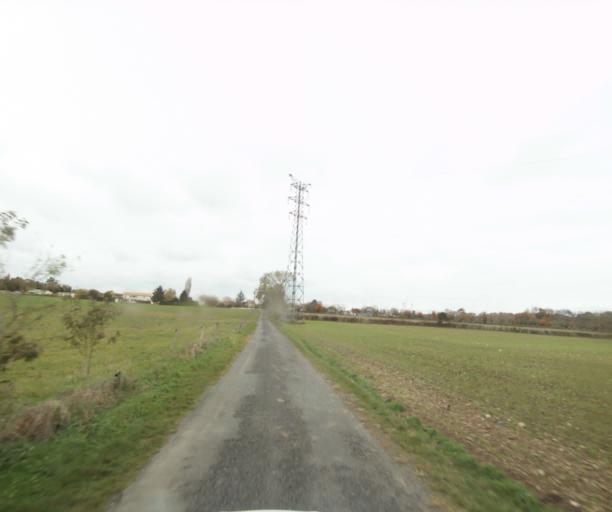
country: FR
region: Poitou-Charentes
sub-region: Departement de la Charente-Maritime
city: Saintes
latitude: 45.7659
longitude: -0.6296
